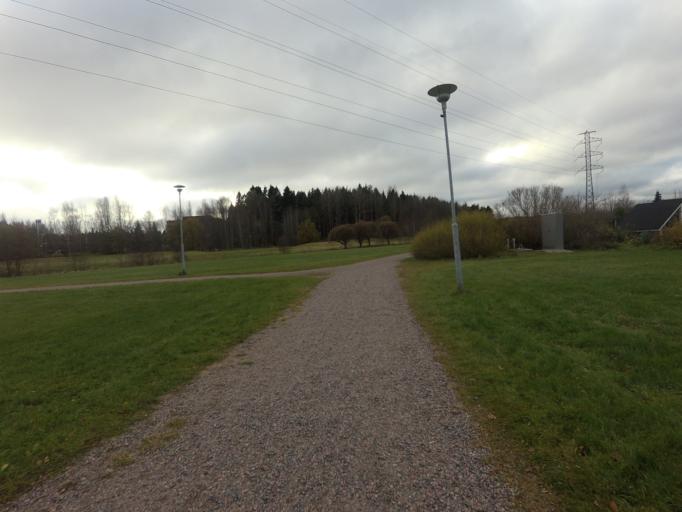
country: FI
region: Uusimaa
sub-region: Helsinki
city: Kauniainen
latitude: 60.1788
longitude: 24.7031
